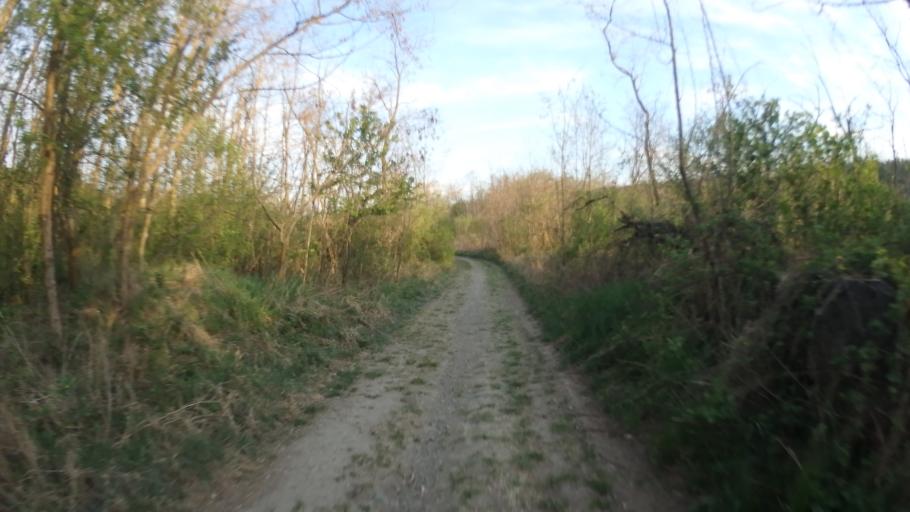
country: CZ
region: South Moravian
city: Zelesice
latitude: 49.1284
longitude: 16.5574
